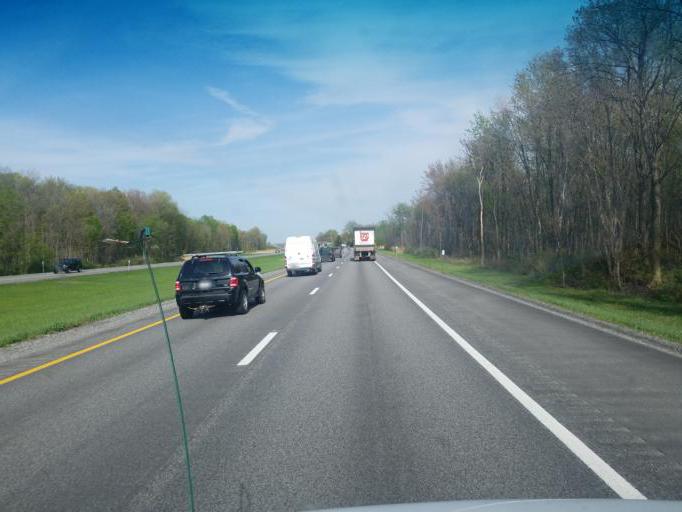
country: US
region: New York
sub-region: Madison County
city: Bolivar
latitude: 43.0912
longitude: -75.9088
